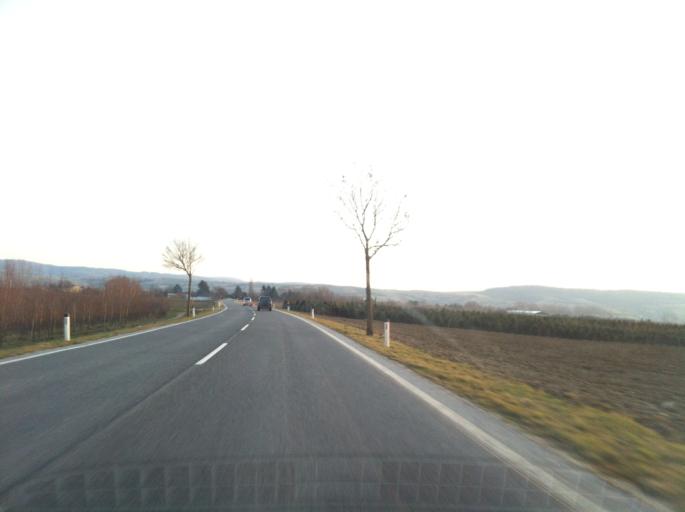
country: AT
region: Lower Austria
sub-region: Politischer Bezirk Tulln
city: Tulln
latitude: 48.3075
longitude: 16.0573
